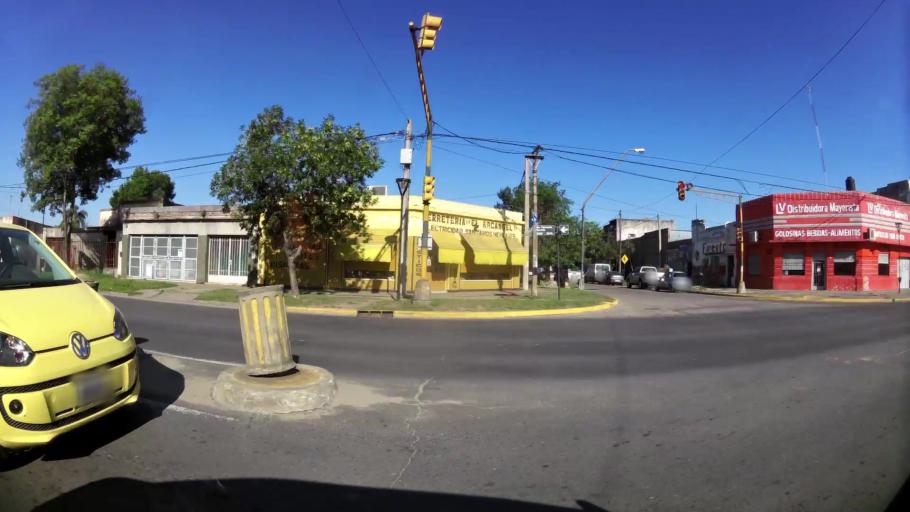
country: AR
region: Santa Fe
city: Santa Fe de la Vera Cruz
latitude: -31.6099
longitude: -60.7043
